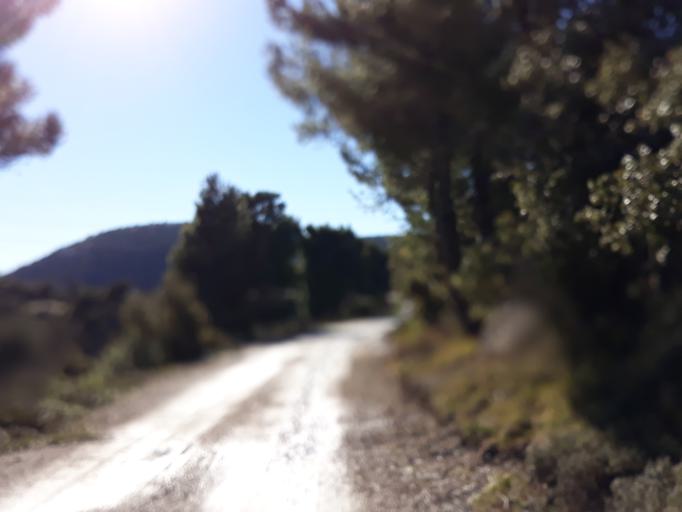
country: GR
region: Attica
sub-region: Nomarchia Dytikis Attikis
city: Fyli
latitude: 38.1451
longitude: 23.6393
